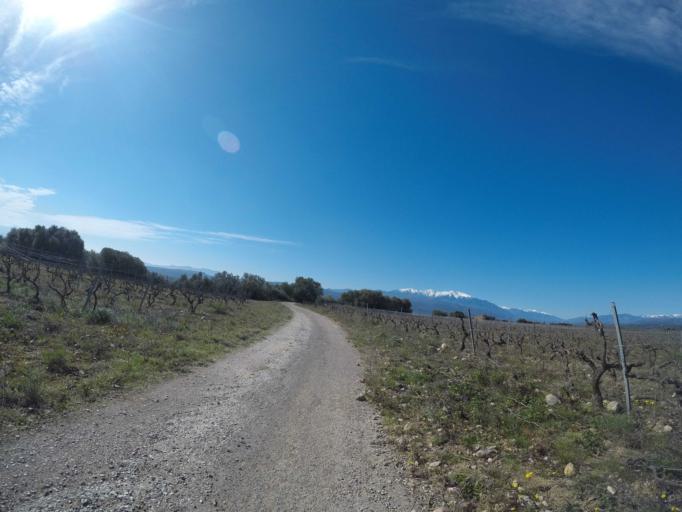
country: FR
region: Languedoc-Roussillon
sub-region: Departement des Pyrenees-Orientales
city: Millas
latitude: 42.7115
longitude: 2.6920
